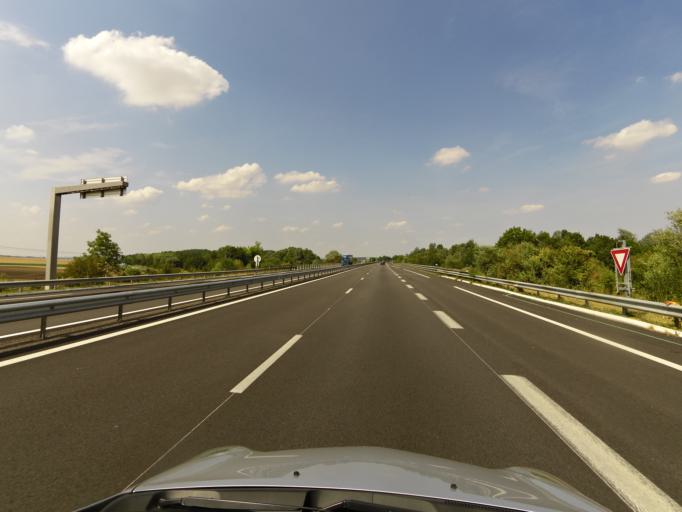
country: FR
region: Champagne-Ardenne
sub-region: Departement de la Marne
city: Loivre
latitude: 49.3600
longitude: 3.9532
